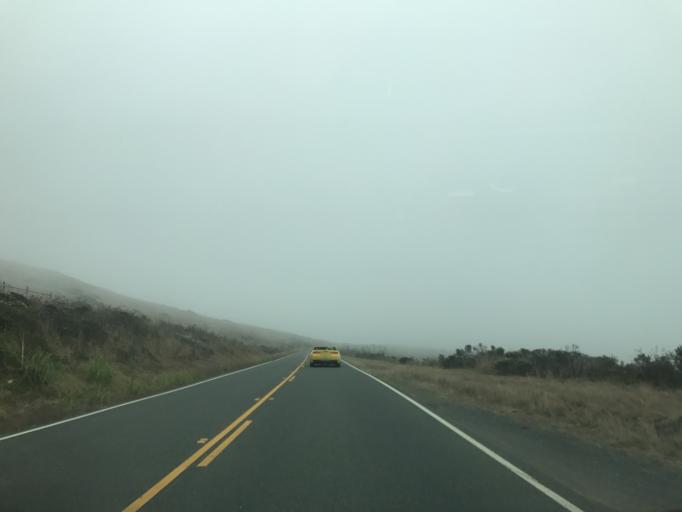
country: US
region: California
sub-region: Sonoma County
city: Monte Rio
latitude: 38.4619
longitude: -123.1460
